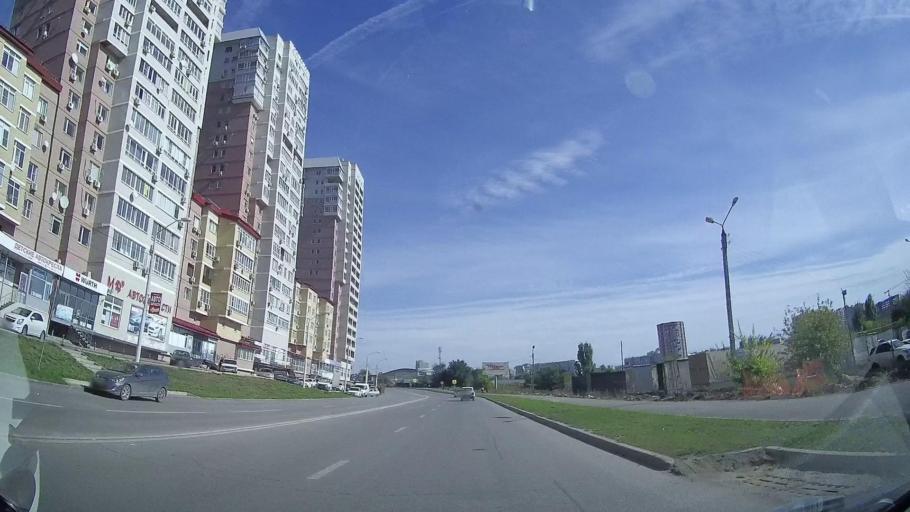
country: RU
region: Rostov
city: Severnyy
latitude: 47.2888
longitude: 39.6956
